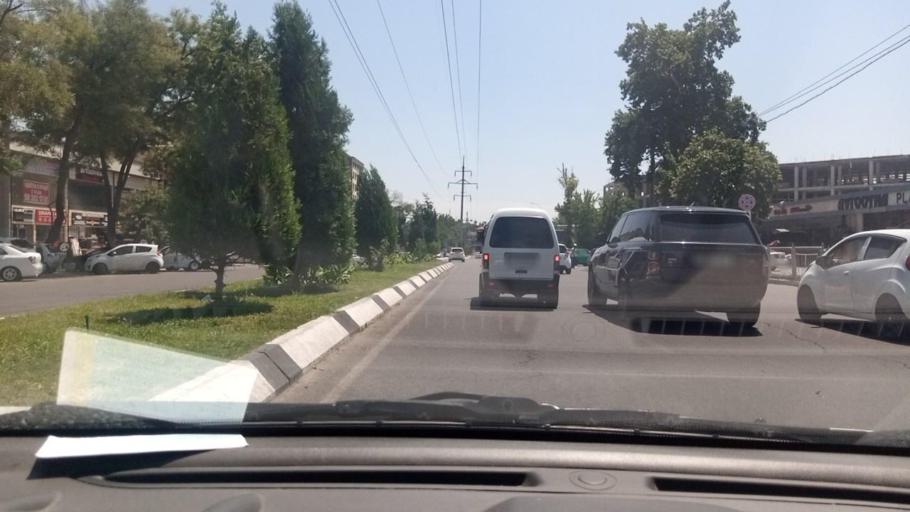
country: UZ
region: Toshkent Shahri
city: Tashkent
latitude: 41.2847
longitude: 69.1945
